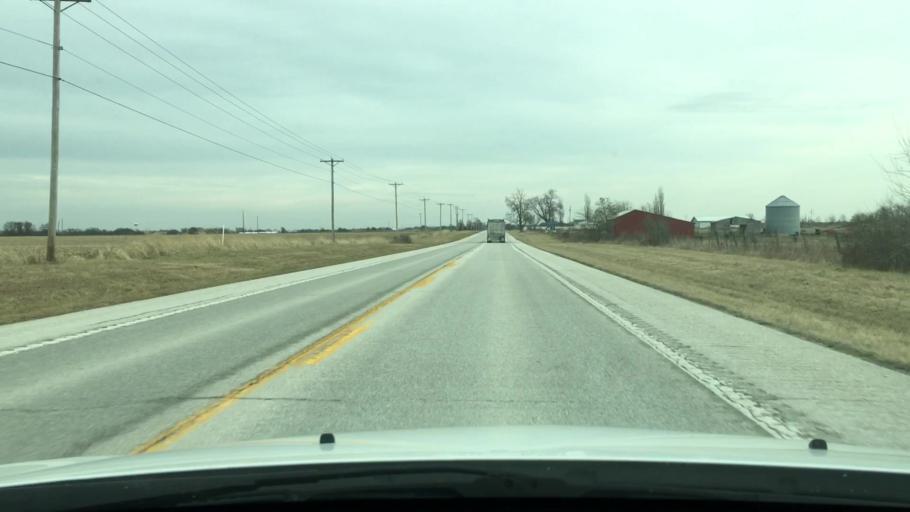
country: US
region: Missouri
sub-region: Pike County
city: Bowling Green
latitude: 39.3443
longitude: -91.2602
